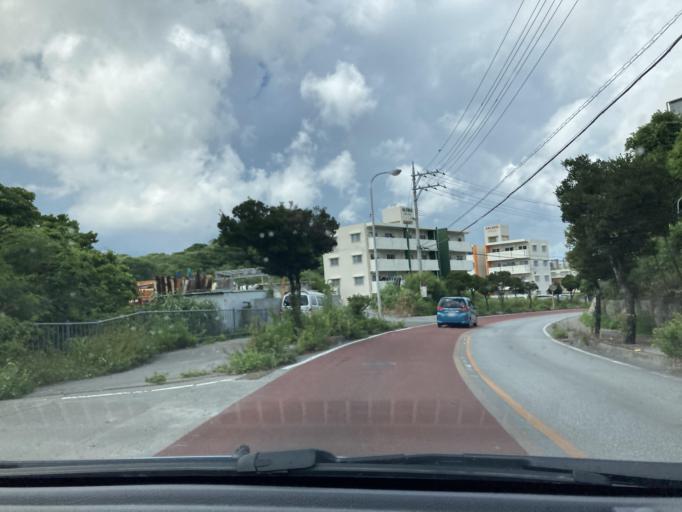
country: JP
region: Okinawa
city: Tomigusuku
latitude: 26.1710
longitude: 127.7531
